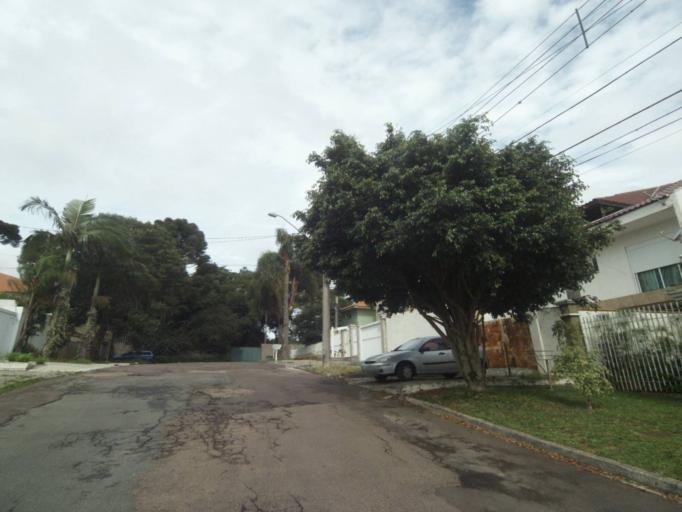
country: BR
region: Parana
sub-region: Curitiba
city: Curitiba
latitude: -25.4446
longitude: -49.3025
